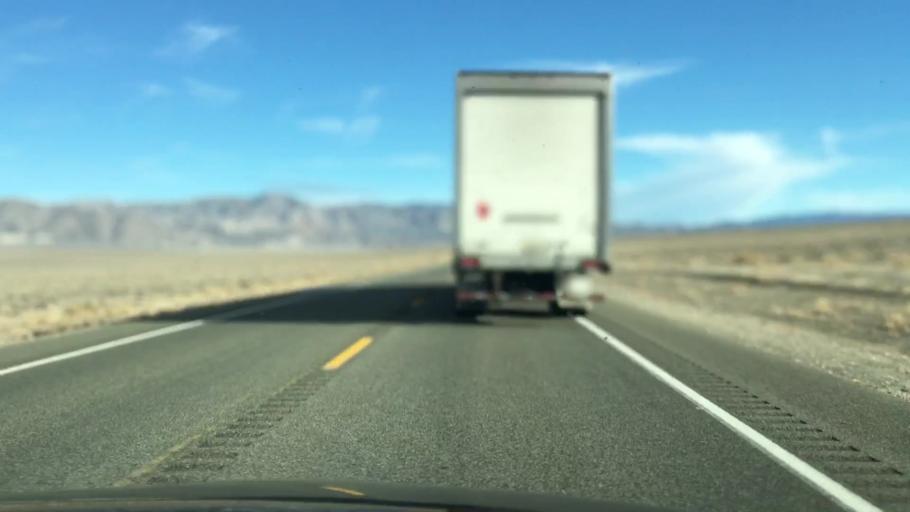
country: US
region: Nevada
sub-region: Mineral County
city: Hawthorne
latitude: 38.5308
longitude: -118.2700
